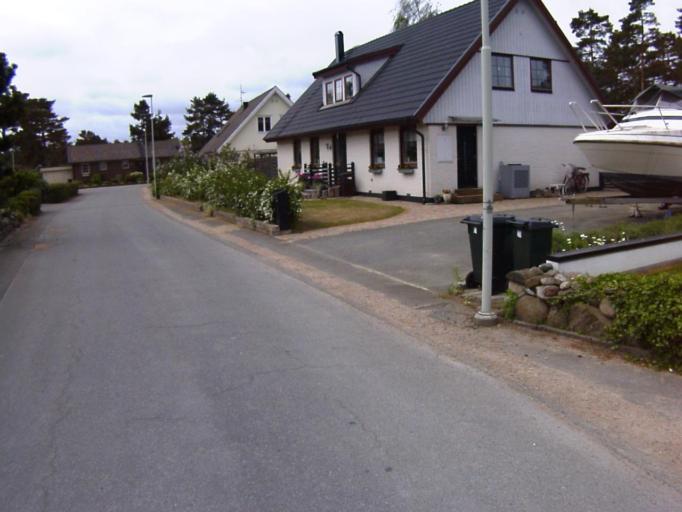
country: SE
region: Skane
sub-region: Kristianstads Kommun
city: Ahus
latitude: 55.9387
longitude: 14.2772
